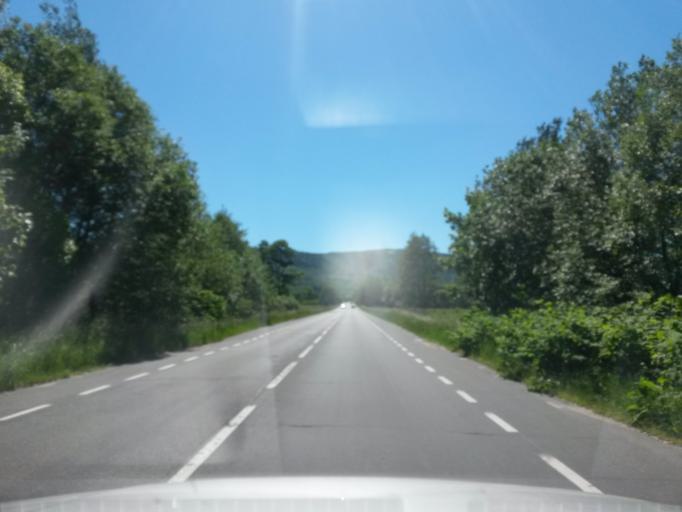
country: PL
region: Lower Silesian Voivodeship
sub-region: Powiat jeleniogorski
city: Kowary
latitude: 50.7972
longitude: 15.8440
